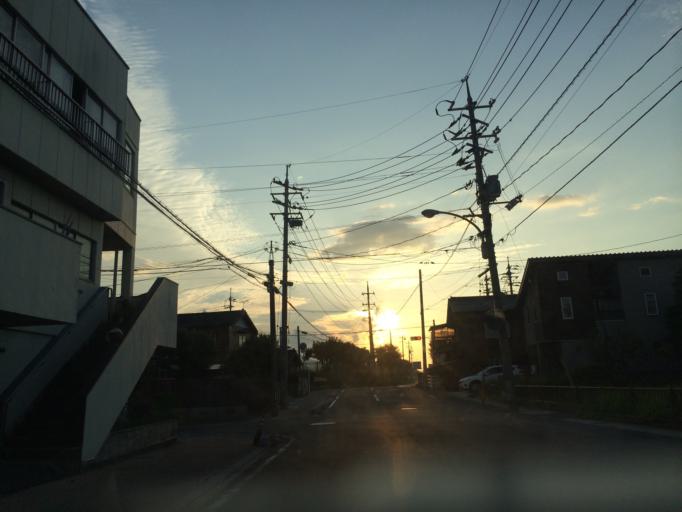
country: JP
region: Shimane
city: Matsue-shi
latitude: 35.4708
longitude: 133.0622
